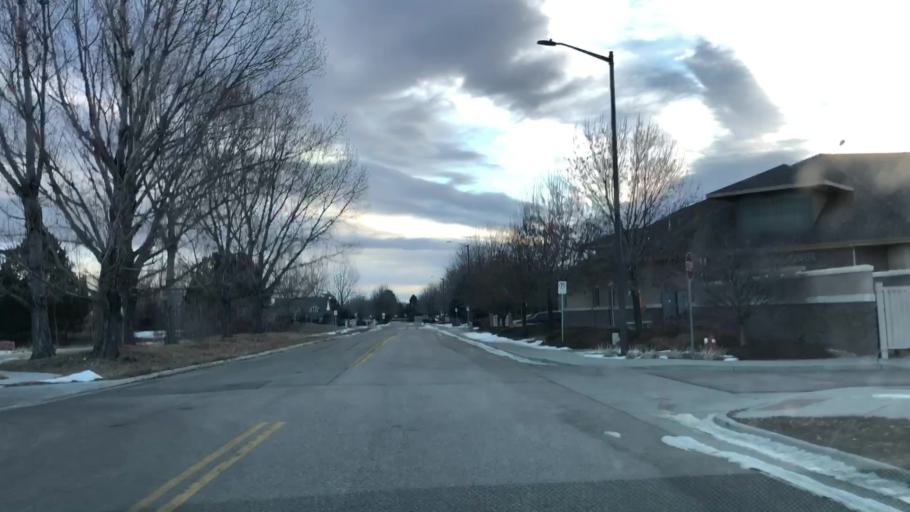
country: US
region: Colorado
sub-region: Larimer County
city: Loveland
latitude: 40.4083
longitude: -105.0246
